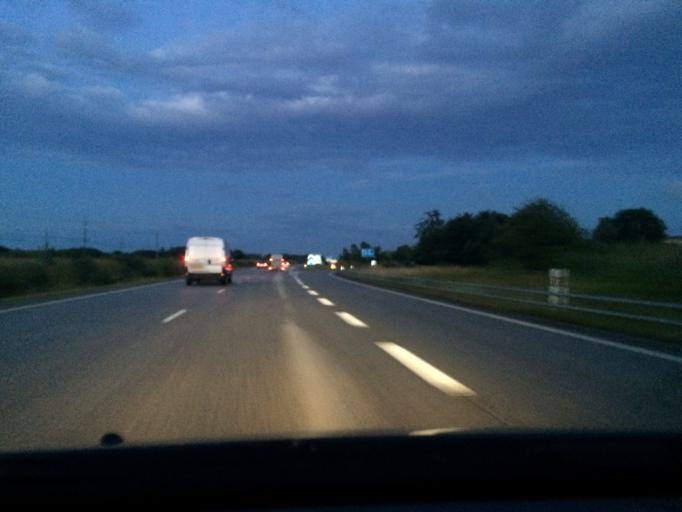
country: SE
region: Skane
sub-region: Malmo
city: Bunkeflostrand
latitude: 55.5613
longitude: 12.9337
